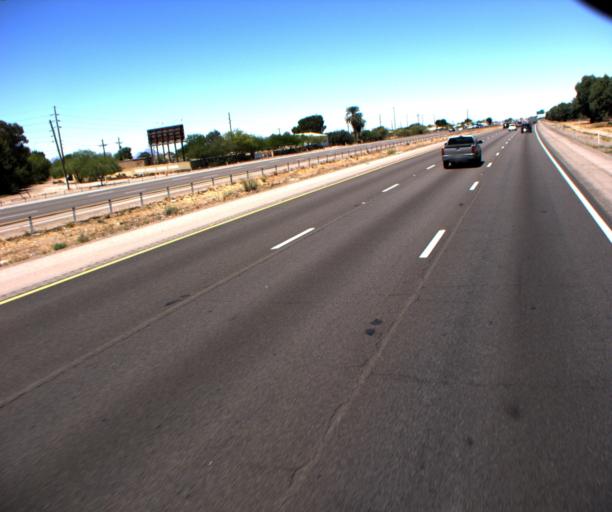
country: US
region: Arizona
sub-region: Pima County
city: Marana
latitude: 32.4136
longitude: -111.1489
